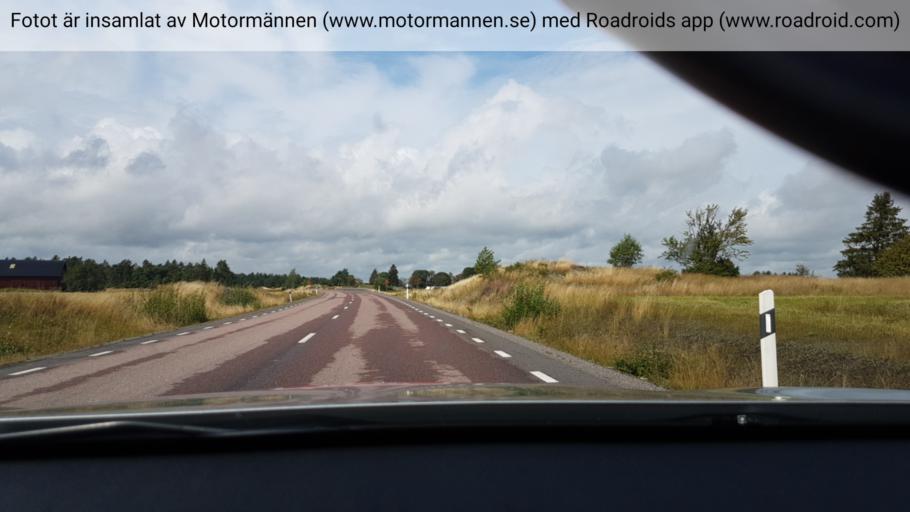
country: SE
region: Uppsala
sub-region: Osthammars Kommun
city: Bjorklinge
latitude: 59.9279
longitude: 17.4943
